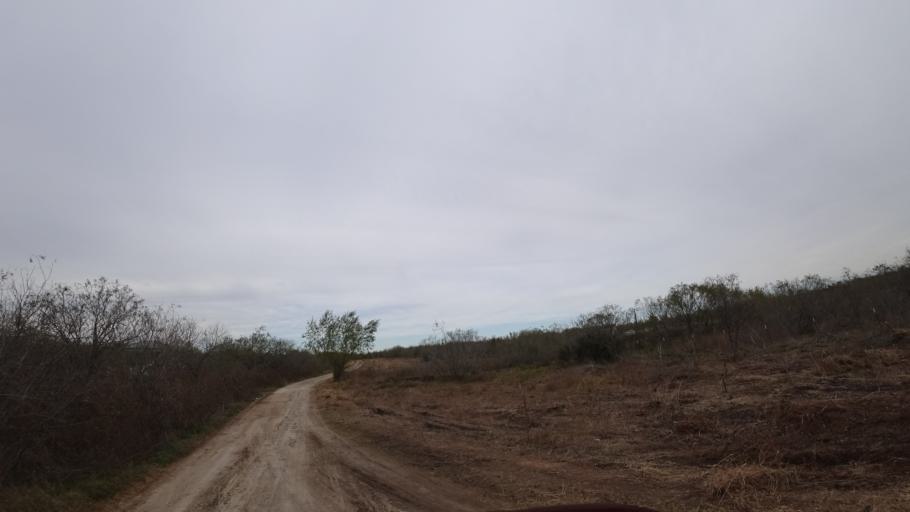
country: US
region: Texas
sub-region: Travis County
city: Garfield
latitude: 30.1059
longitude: -97.5845
